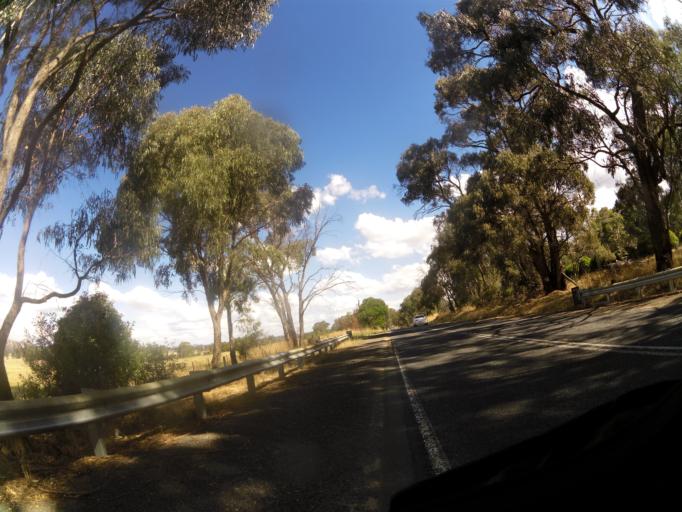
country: AU
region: Victoria
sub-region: Mansfield
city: Mansfield
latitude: -36.9257
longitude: 146.0017
